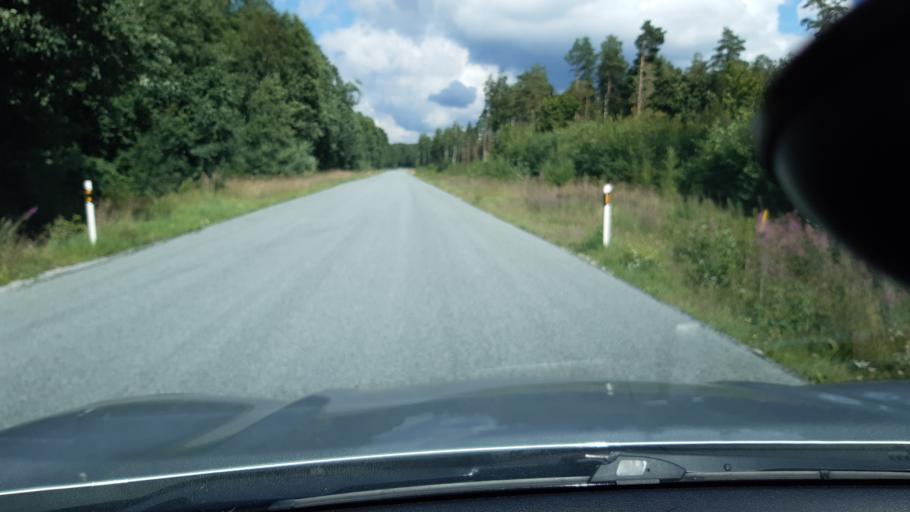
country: EE
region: Raplamaa
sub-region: Kehtna vald
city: Kehtna
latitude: 58.8800
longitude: 25.0198
